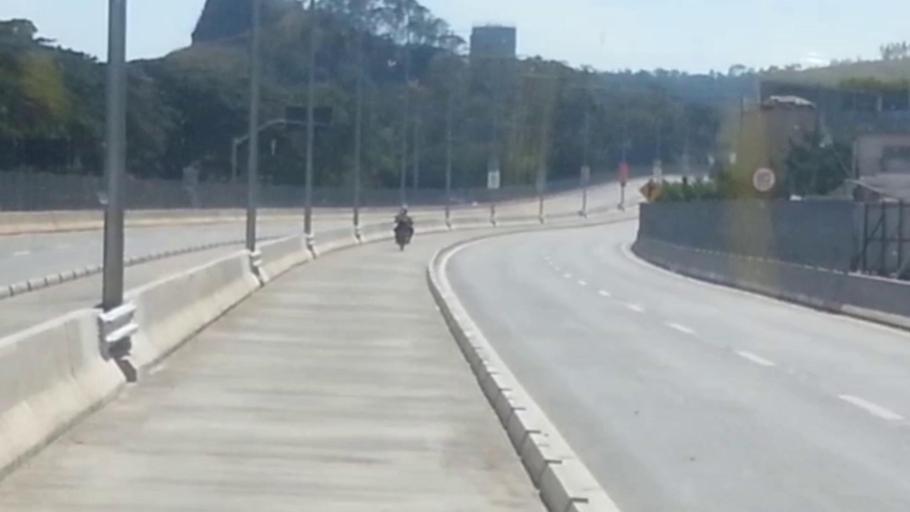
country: BR
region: Rio de Janeiro
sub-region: Nilopolis
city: Nilopolis
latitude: -22.8937
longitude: -43.3998
